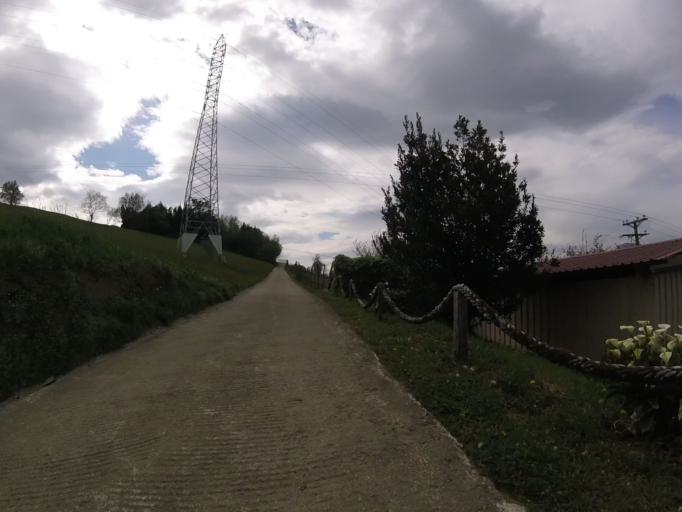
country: ES
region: Basque Country
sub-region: Provincia de Guipuzcoa
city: Aizarnazabal
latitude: 43.2487
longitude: -2.1948
